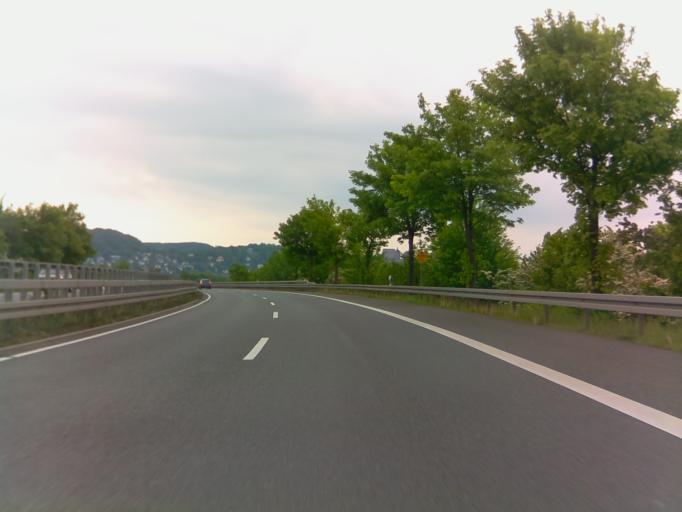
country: DE
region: Hesse
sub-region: Regierungsbezirk Giessen
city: Marburg an der Lahn
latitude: 50.7777
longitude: 8.7601
